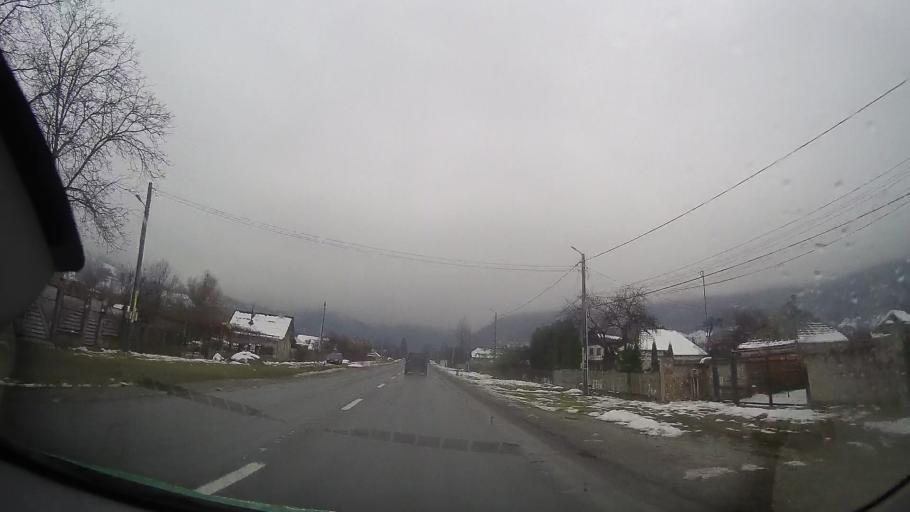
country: RO
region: Neamt
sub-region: Comuna Pangarati
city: Stejaru
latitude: 46.9069
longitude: 26.1768
